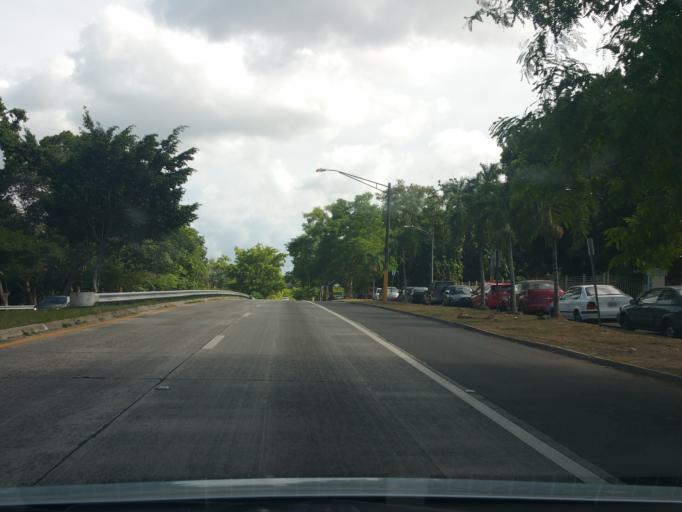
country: PR
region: Trujillo Alto
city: Trujillo Alto
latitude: 18.3871
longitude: -66.0300
